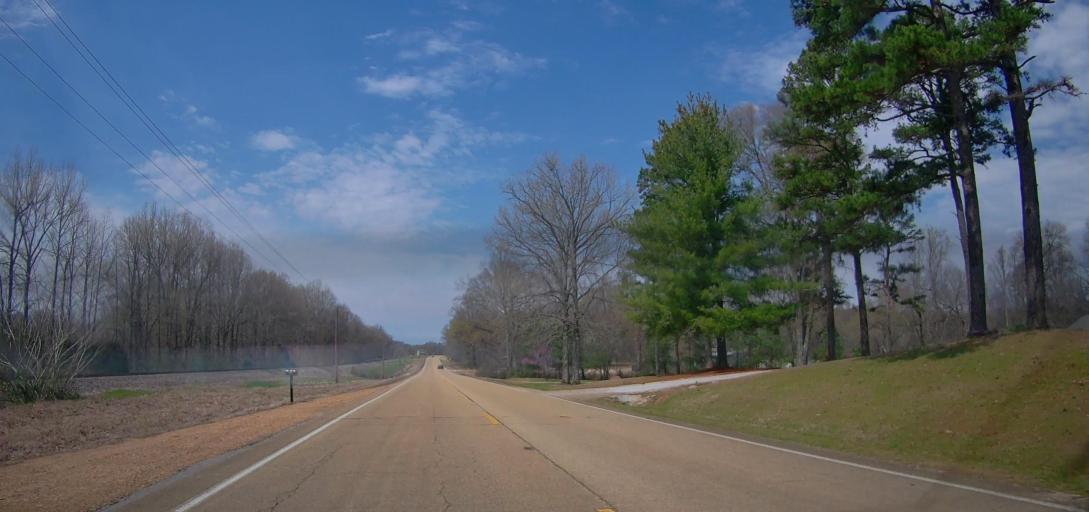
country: US
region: Mississippi
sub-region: Benton County
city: Ashland
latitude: 34.6286
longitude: -89.2656
